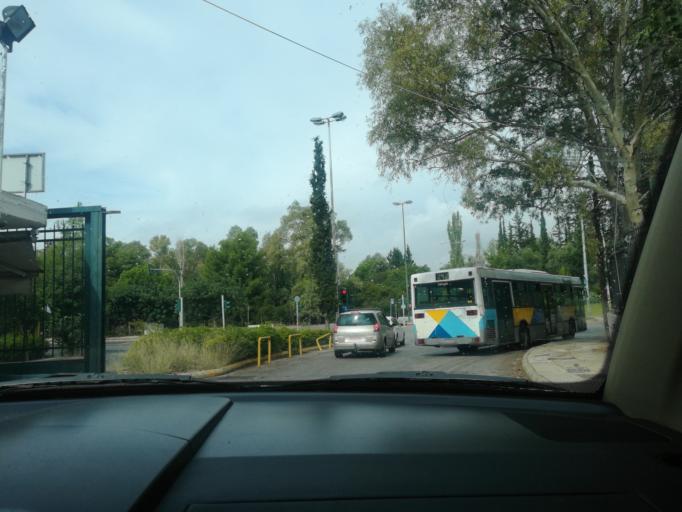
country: GR
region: Attica
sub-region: Nomarchia Athinas
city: Papagou
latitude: 37.9823
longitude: 23.7811
